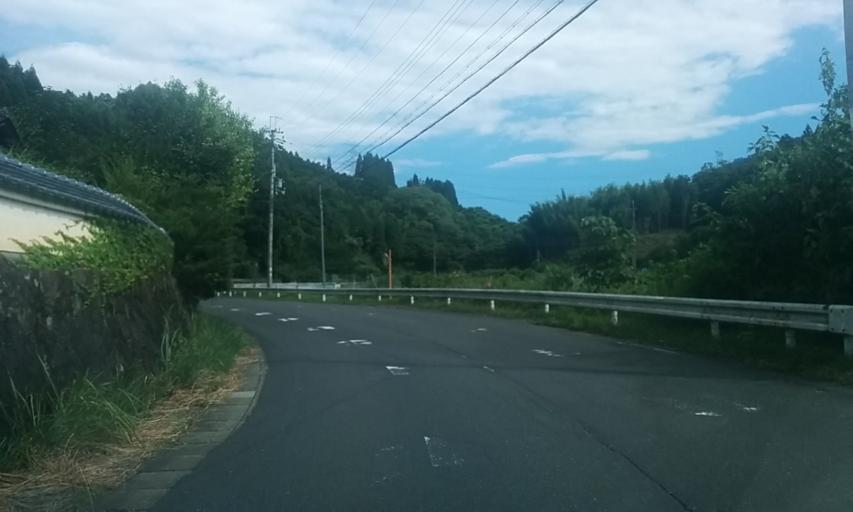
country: JP
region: Kyoto
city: Fukuchiyama
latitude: 35.3640
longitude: 135.1329
